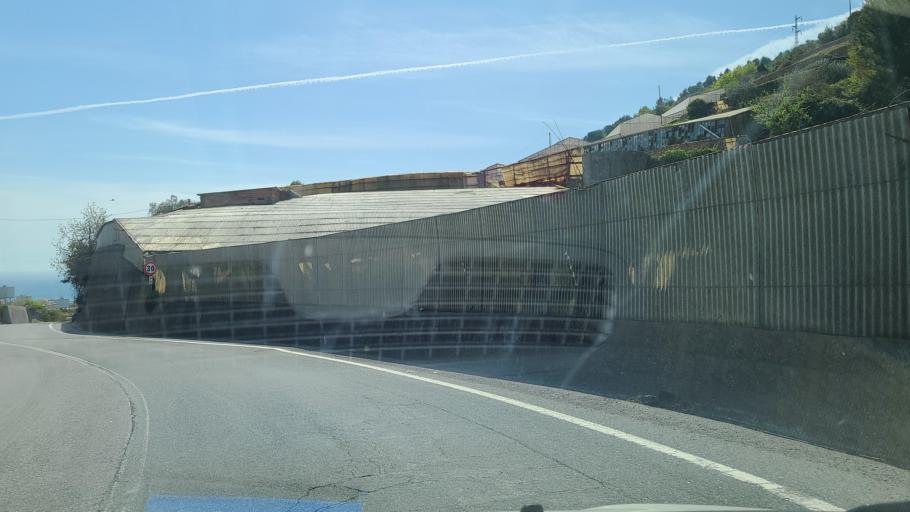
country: IT
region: Liguria
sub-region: Provincia di Imperia
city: Taggia
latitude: 43.8459
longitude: 7.8412
